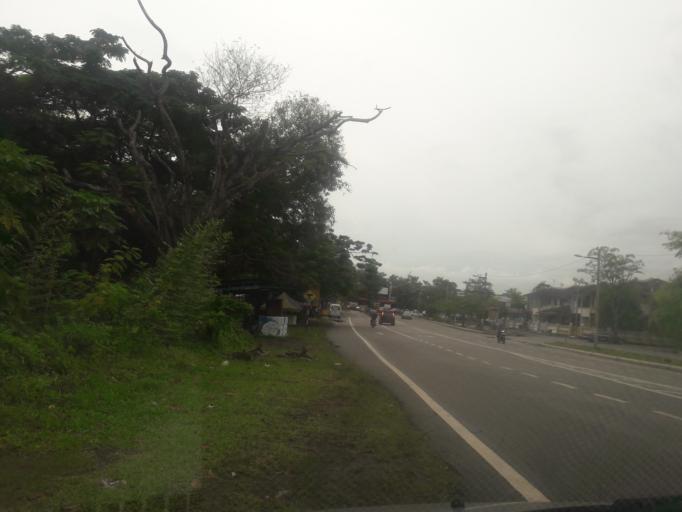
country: MY
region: Kedah
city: Sungai Petani
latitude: 5.6594
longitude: 100.4851
